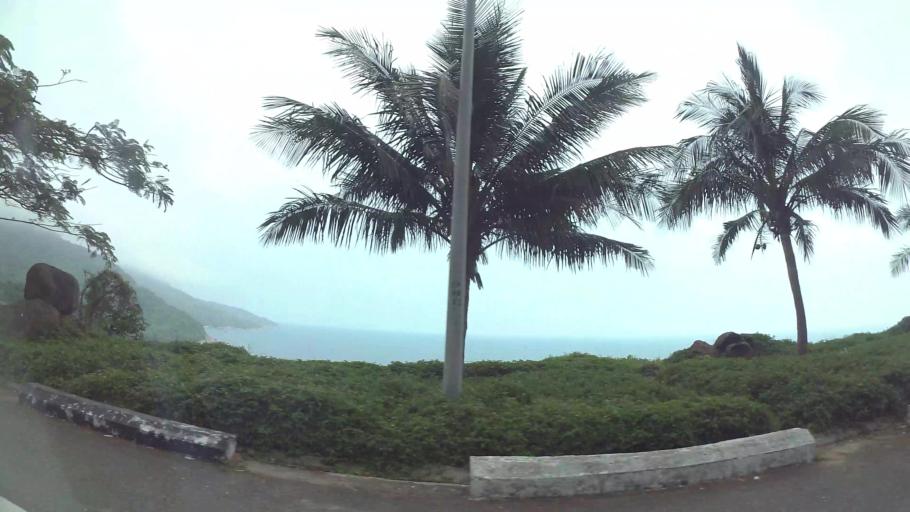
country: VN
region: Da Nang
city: Son Tra
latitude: 16.1093
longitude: 108.3085
